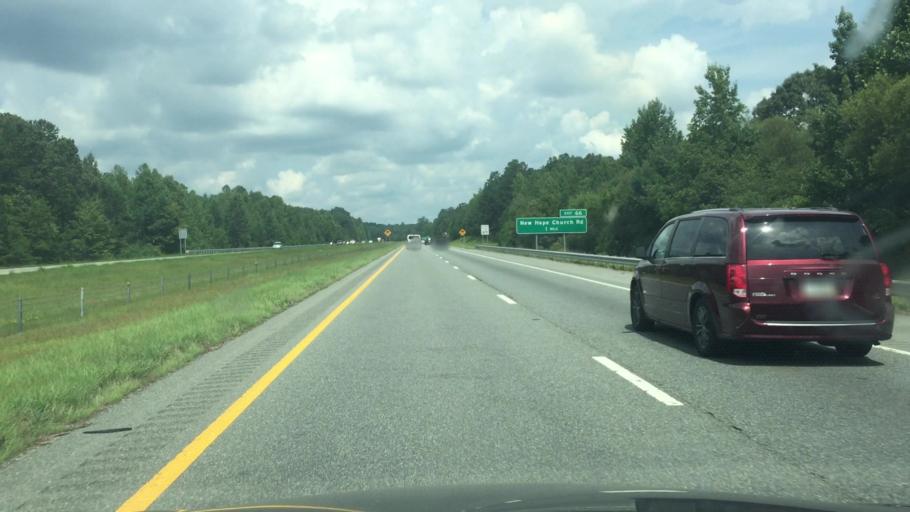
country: US
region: North Carolina
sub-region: Randolph County
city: Asheboro
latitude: 35.5749
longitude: -79.8058
